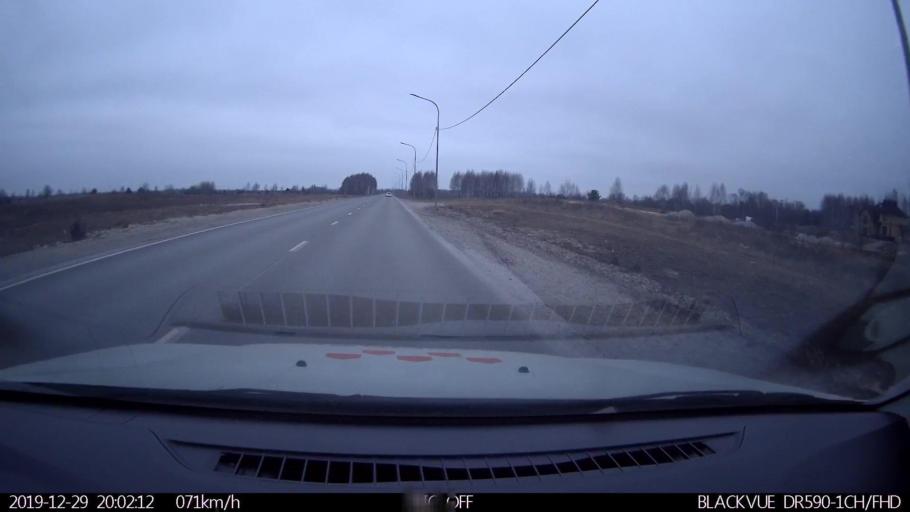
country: RU
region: Nizjnij Novgorod
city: Bor
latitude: 56.3631
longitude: 44.0326
